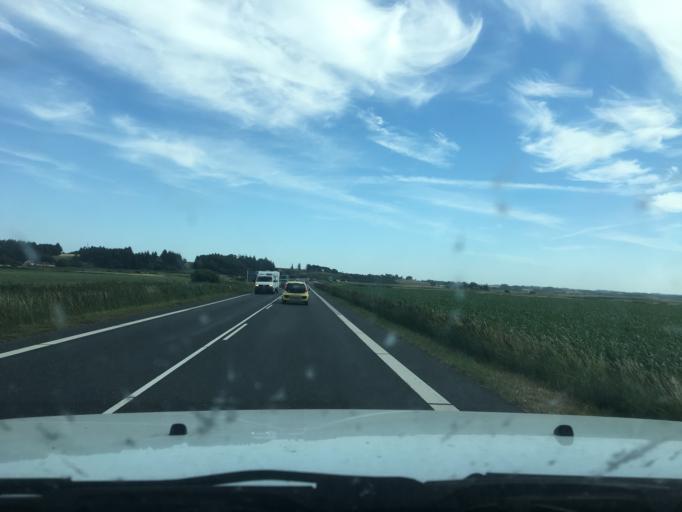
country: DK
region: Central Jutland
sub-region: Viborg Kommune
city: Viborg
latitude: 56.5748
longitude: 9.3778
